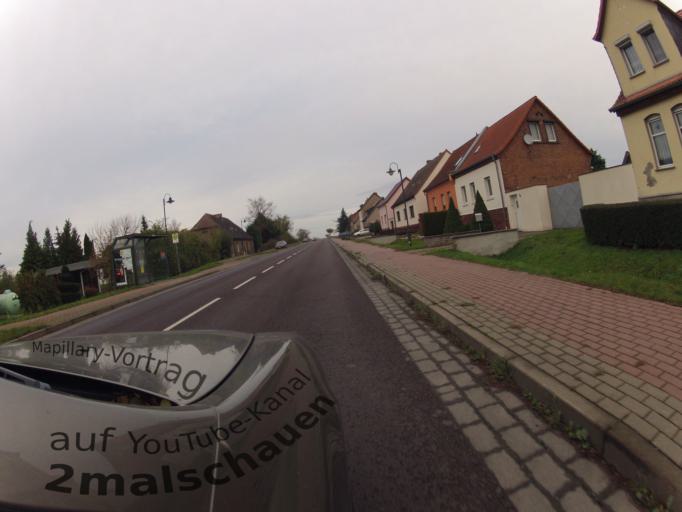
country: DE
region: Saxony-Anhalt
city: Konnern
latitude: 51.7071
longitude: 11.7649
